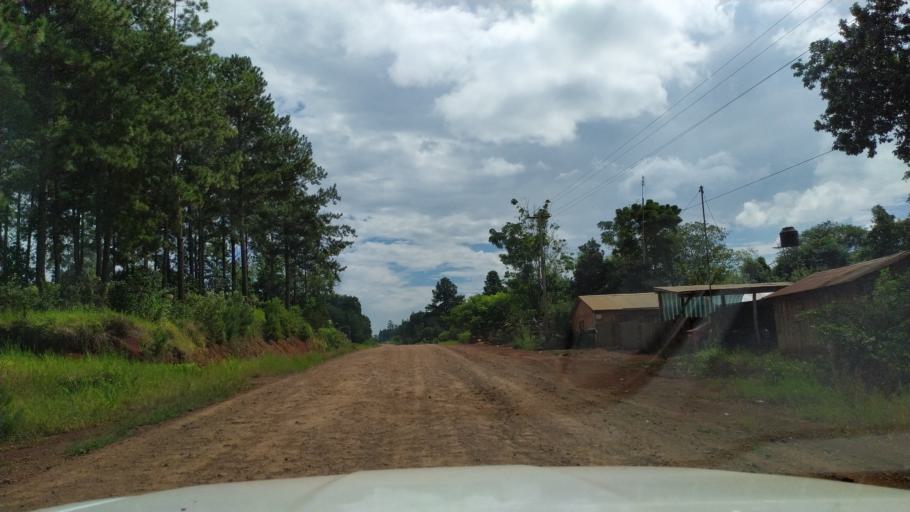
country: AR
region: Misiones
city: Puerto Piray
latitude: -26.5349
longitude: -54.6593
